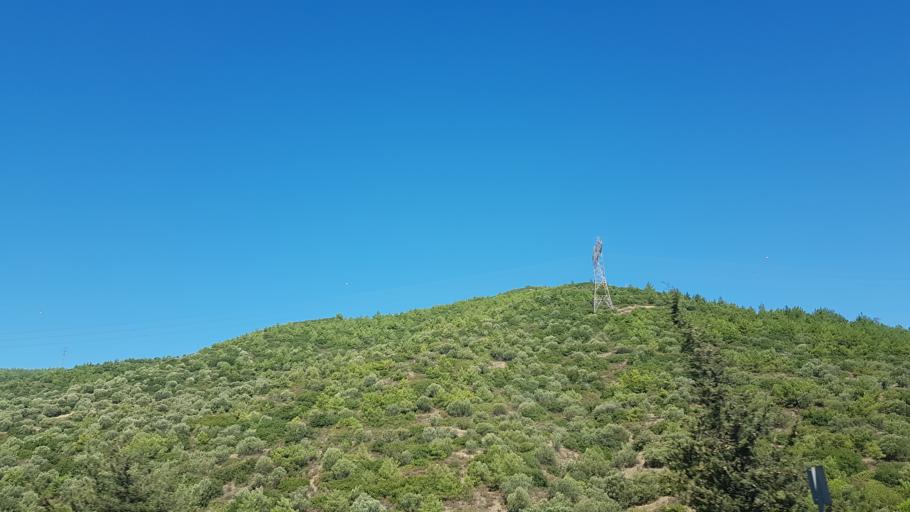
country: TR
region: Izmir
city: Buca
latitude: 38.4035
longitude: 27.2311
